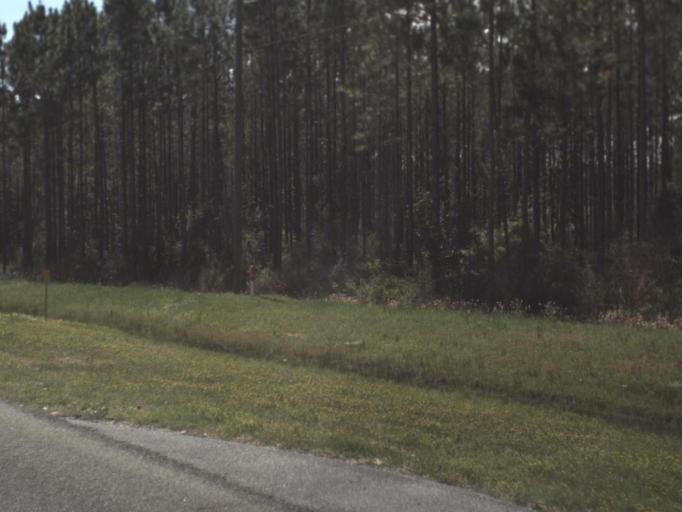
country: US
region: Florida
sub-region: Bay County
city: Laguna Beach
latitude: 30.3064
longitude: -85.8530
